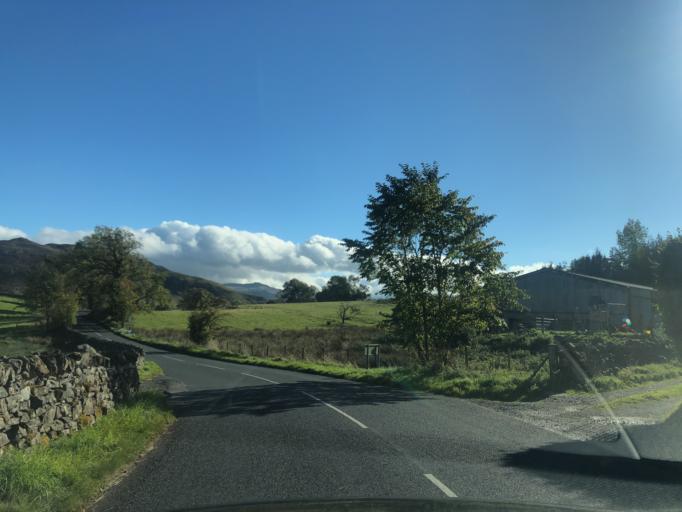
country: GB
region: England
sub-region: Cumbria
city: Ambleside
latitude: 54.6028
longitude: -2.9371
